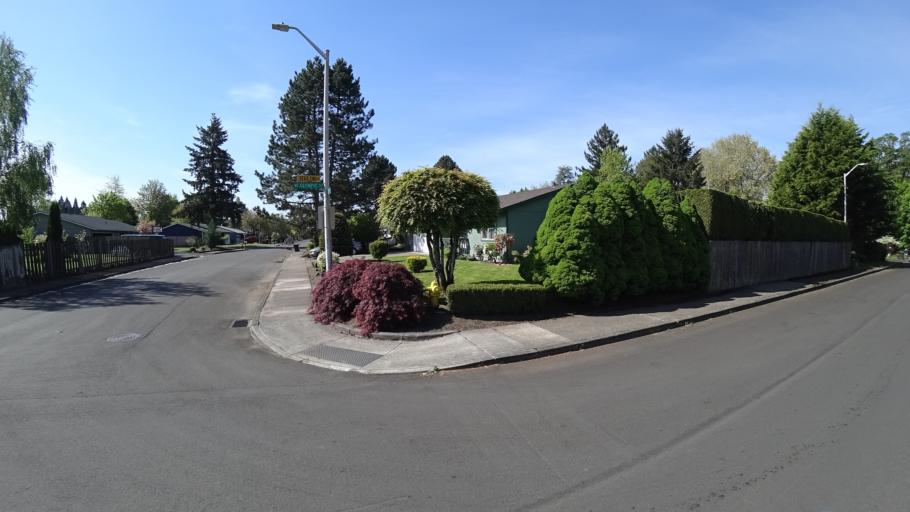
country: US
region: Oregon
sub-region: Washington County
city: Hillsboro
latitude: 45.5261
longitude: -122.9470
